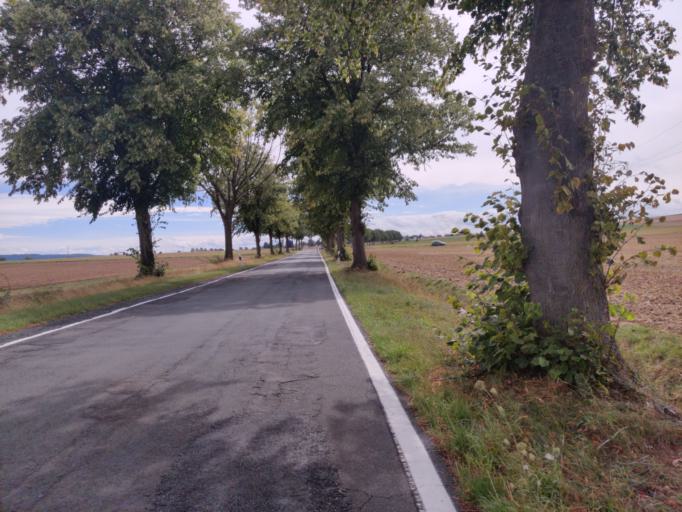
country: DE
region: Lower Saxony
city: Alt Wallmoden
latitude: 52.0159
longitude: 10.3336
